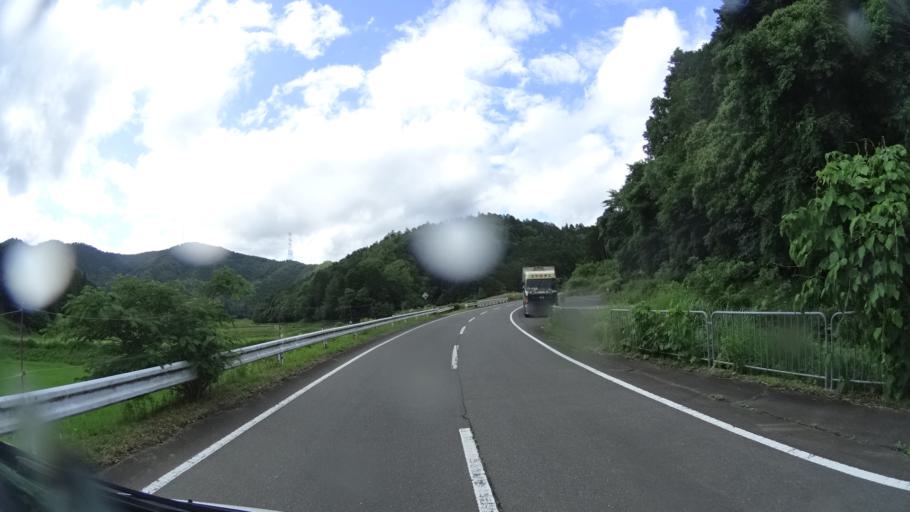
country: JP
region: Kyoto
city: Ayabe
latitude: 35.3500
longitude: 135.1978
